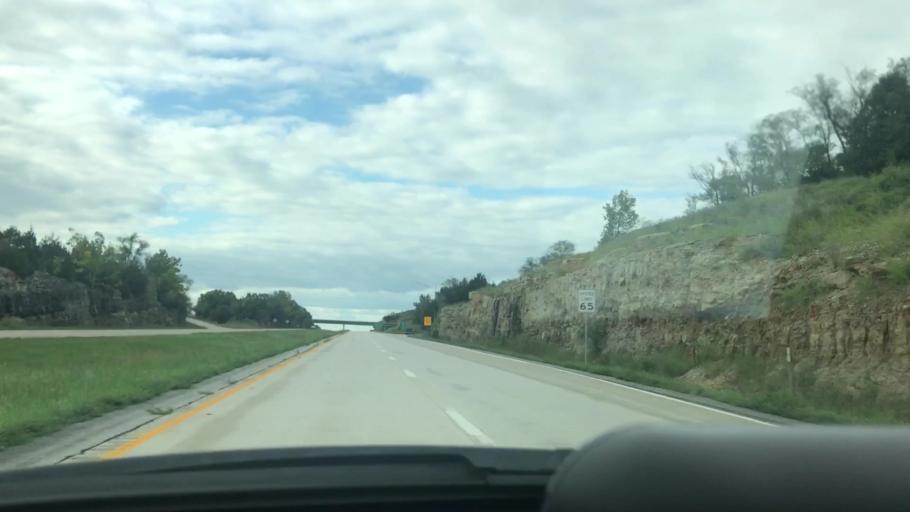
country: US
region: Missouri
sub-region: Benton County
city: Warsaw
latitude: 38.2489
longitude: -93.3615
